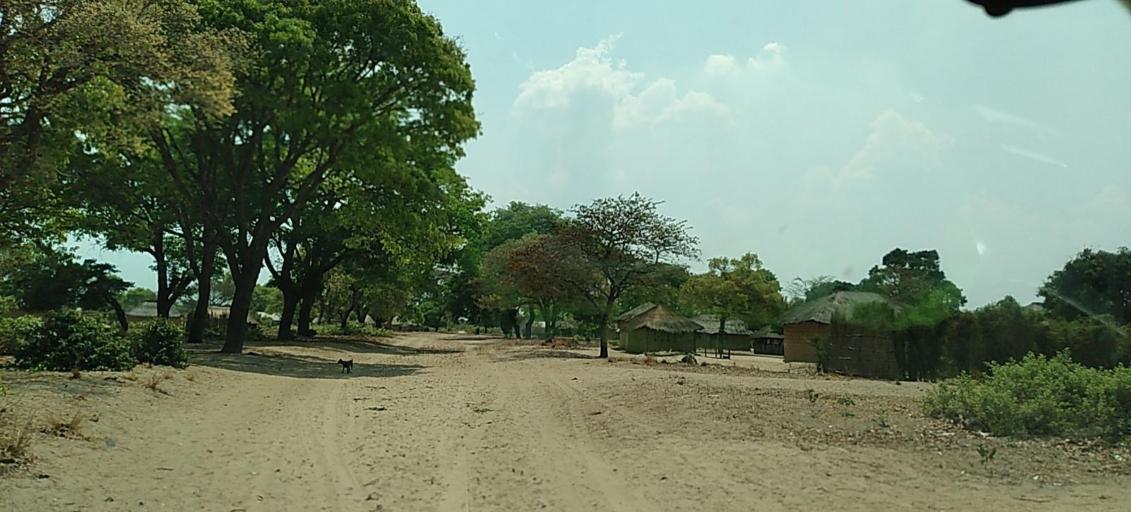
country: ZM
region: North-Western
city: Kabompo
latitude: -13.4016
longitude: 23.8197
